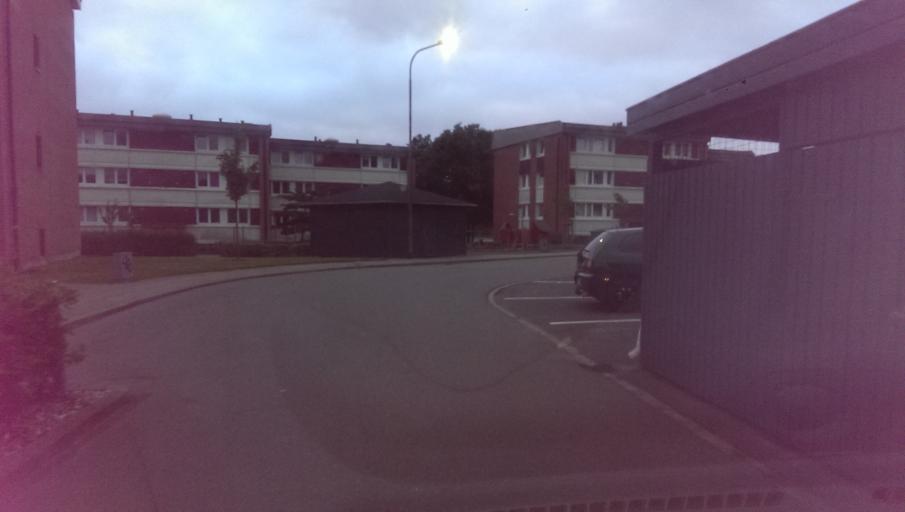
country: DK
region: South Denmark
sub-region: Esbjerg Kommune
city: Esbjerg
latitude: 55.4729
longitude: 8.4892
